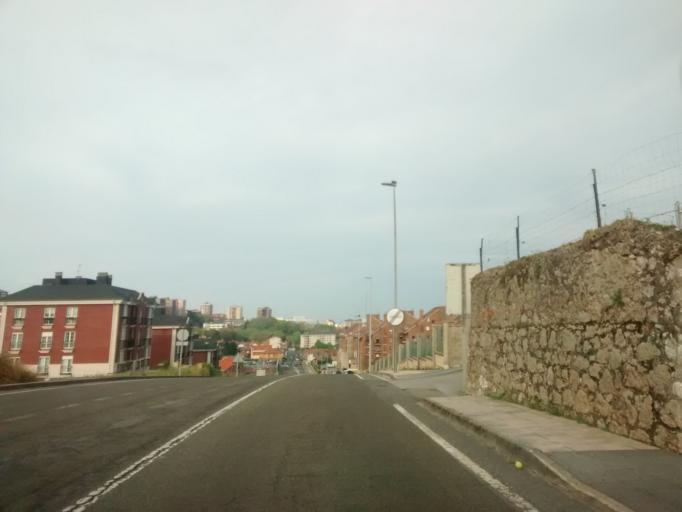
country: ES
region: Cantabria
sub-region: Provincia de Cantabria
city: Santander
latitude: 43.4529
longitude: -3.8519
